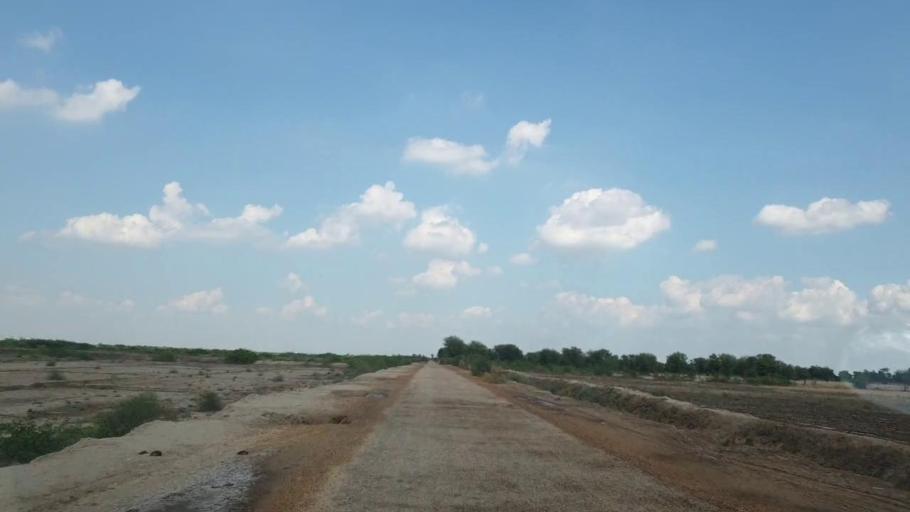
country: PK
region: Sindh
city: Pithoro
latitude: 25.6060
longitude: 69.3619
